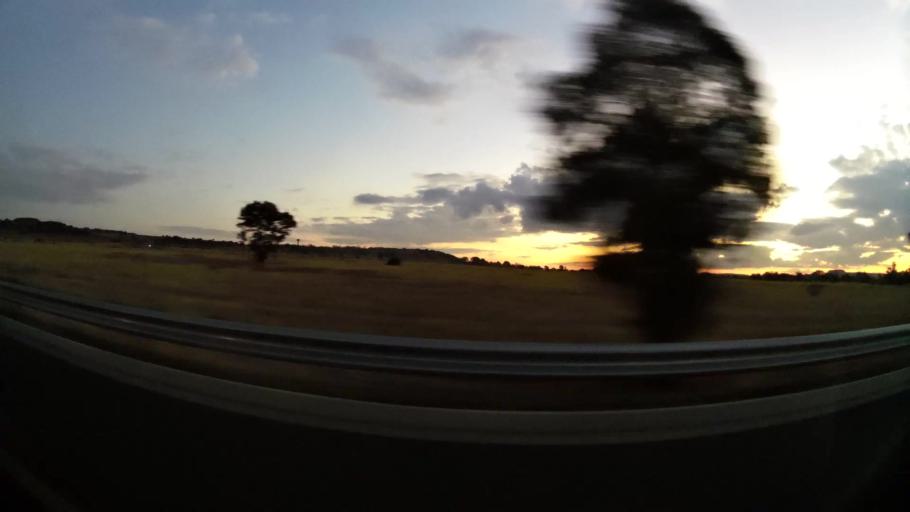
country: ZA
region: Orange Free State
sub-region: Mangaung Metropolitan Municipality
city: Bloemfontein
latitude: -29.1365
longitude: 26.1670
